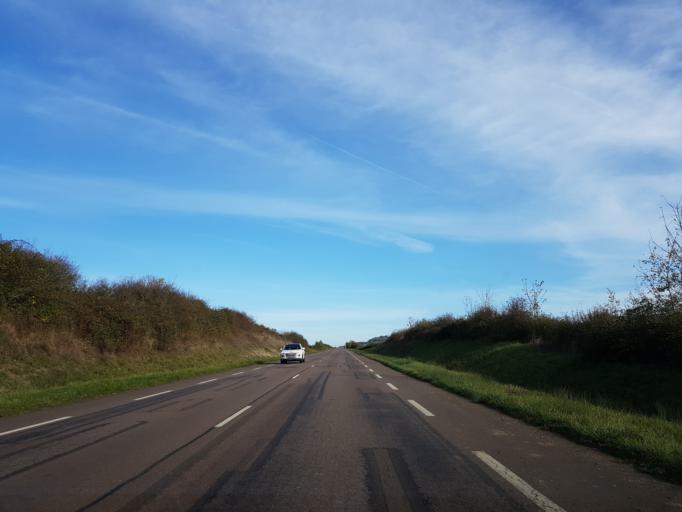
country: FR
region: Bourgogne
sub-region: Departement de la Cote-d'Or
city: Vitteaux
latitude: 47.3925
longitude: 4.4613
